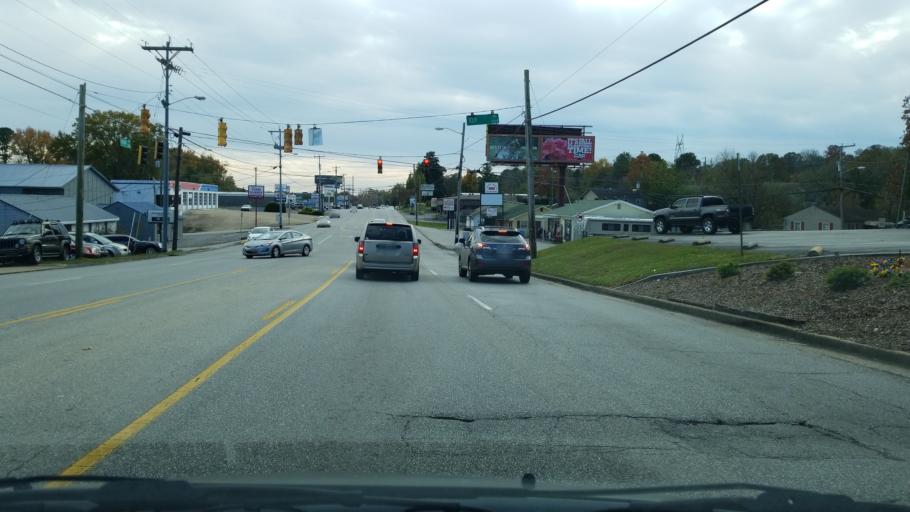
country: US
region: Tennessee
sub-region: Hamilton County
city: Red Bank
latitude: 35.1234
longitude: -85.2481
